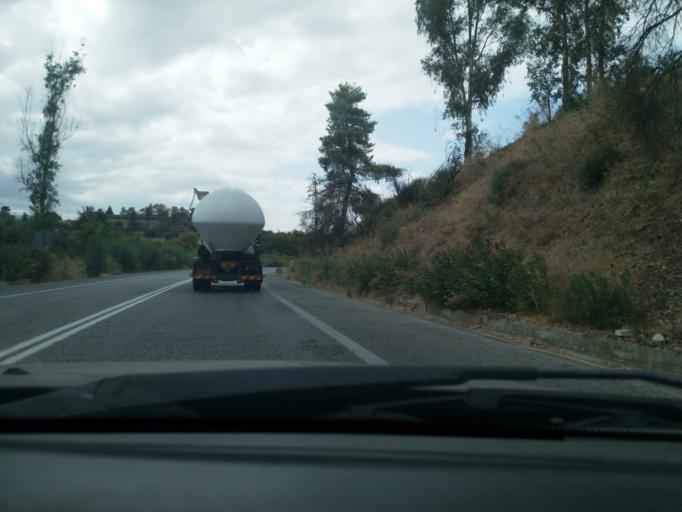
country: GR
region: Crete
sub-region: Nomos Chanias
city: Georgioupolis
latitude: 35.3798
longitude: 24.2011
